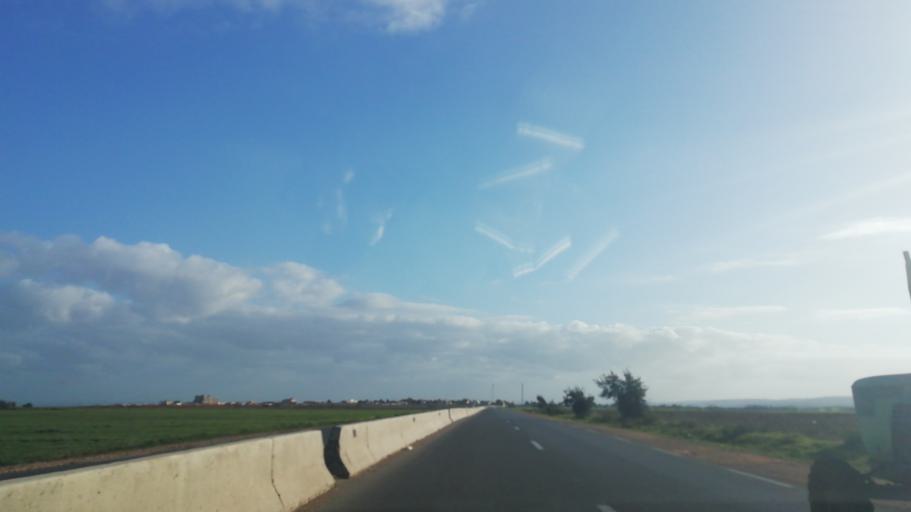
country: DZ
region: Mostaganem
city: Mostaganem
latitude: 36.1082
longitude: 0.3093
